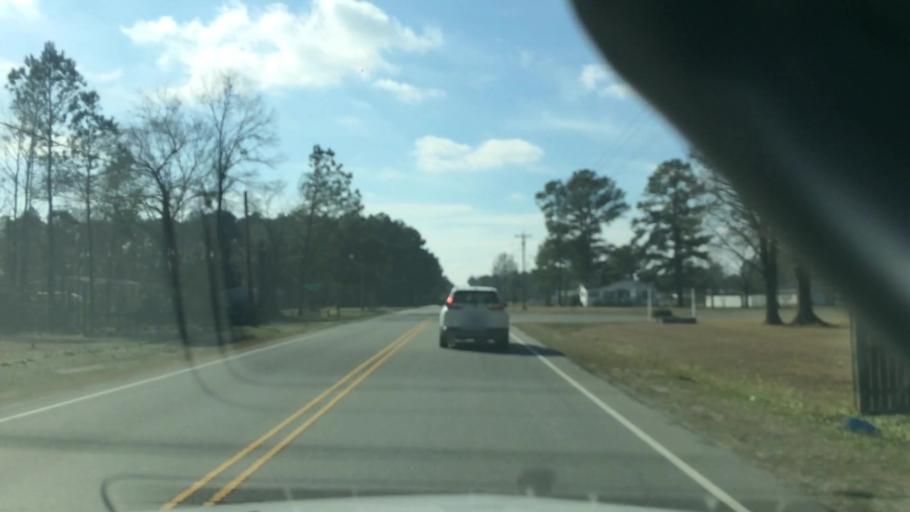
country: US
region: North Carolina
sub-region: Duplin County
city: Wallace
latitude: 34.7744
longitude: -77.9183
